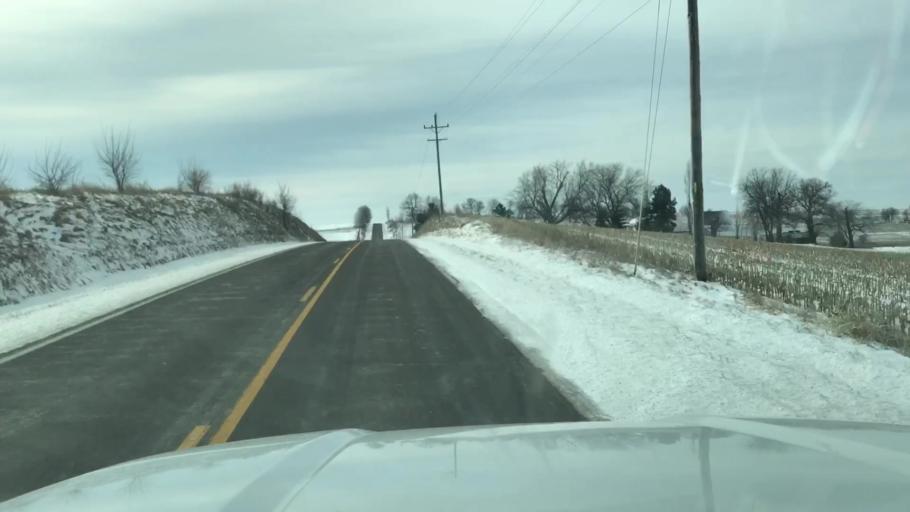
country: US
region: Missouri
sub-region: Holt County
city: Oregon
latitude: 40.0771
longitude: -95.1356
